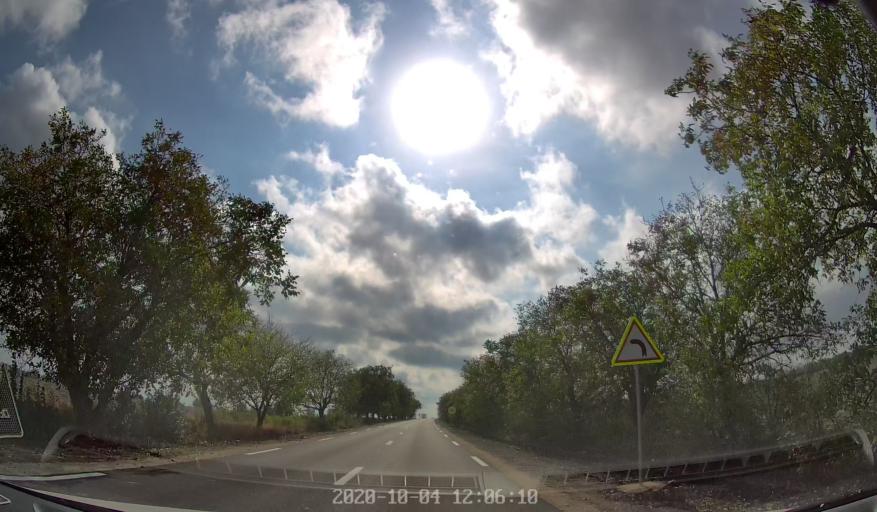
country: MD
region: Rezina
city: Saharna
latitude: 47.5859
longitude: 28.9552
